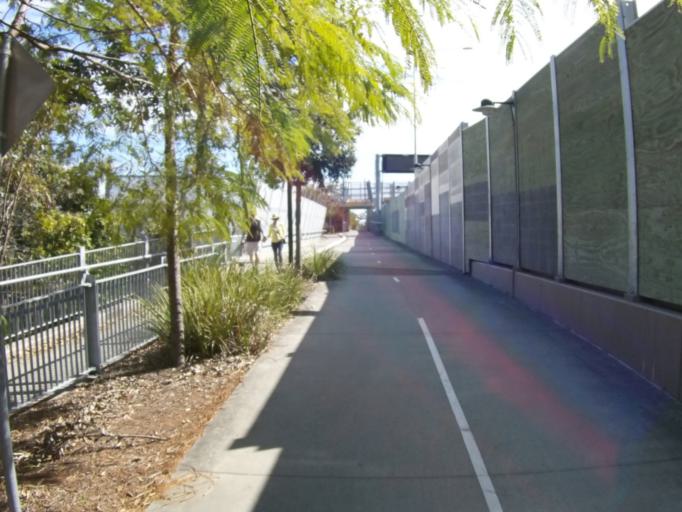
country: AU
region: Queensland
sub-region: Brisbane
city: Woolloongabba
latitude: -27.4971
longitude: 153.0383
